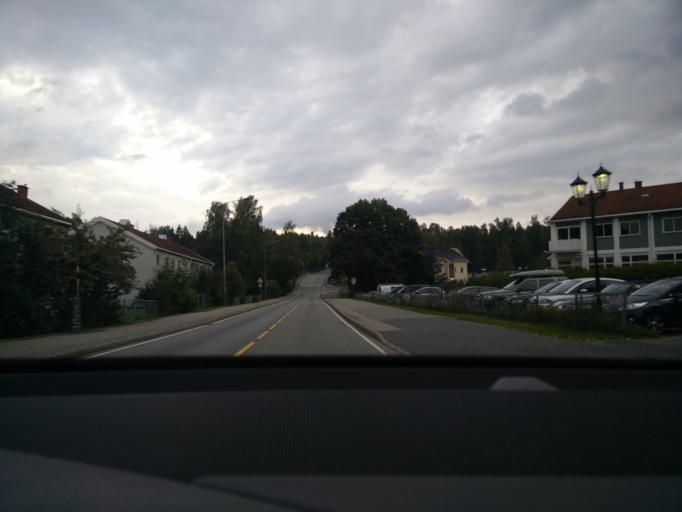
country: NO
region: Akershus
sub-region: Baerum
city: Lysaker
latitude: 59.9357
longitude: 10.6096
